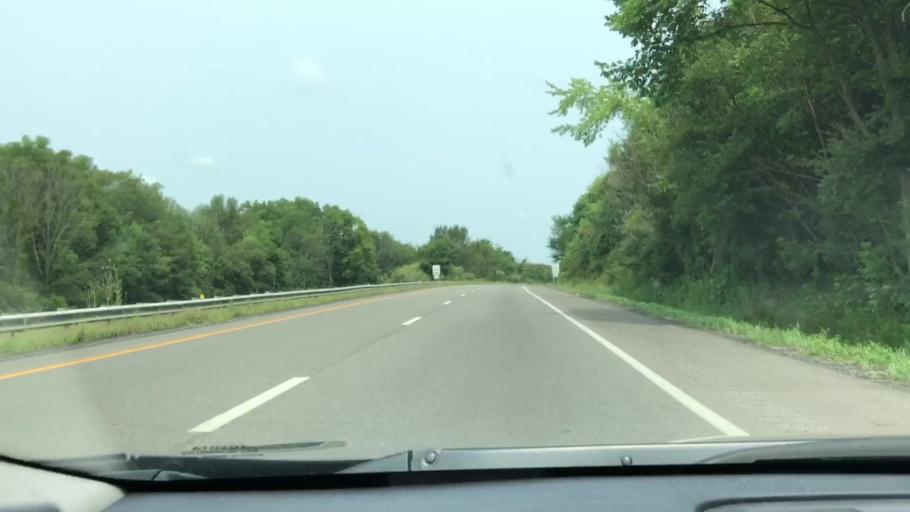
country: US
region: Ohio
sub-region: Summit County
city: Norton
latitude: 41.0715
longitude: -81.6648
